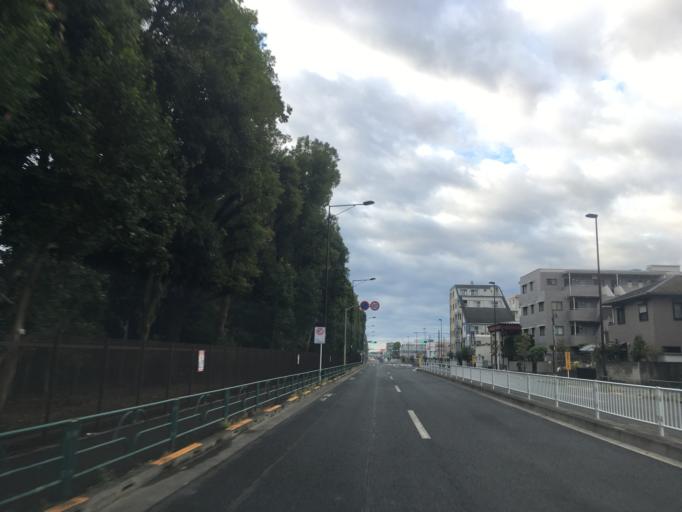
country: JP
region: Tokyo
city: Higashimurayama-shi
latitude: 35.7411
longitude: 139.4665
